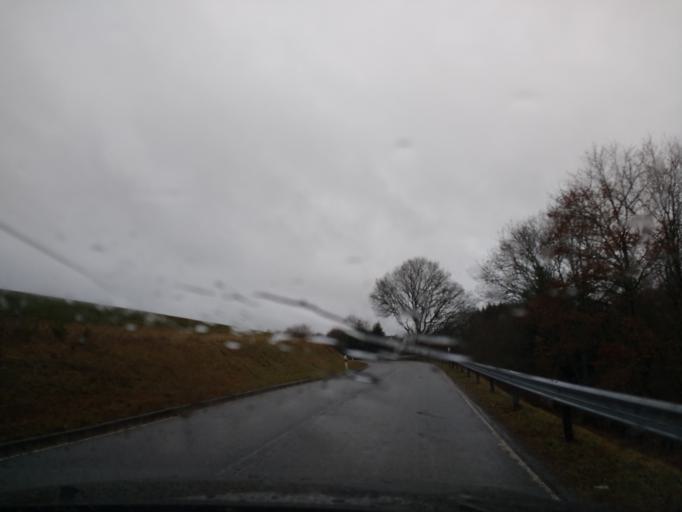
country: DE
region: Rheinland-Pfalz
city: Geisfeld
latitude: 49.7191
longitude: 6.9592
